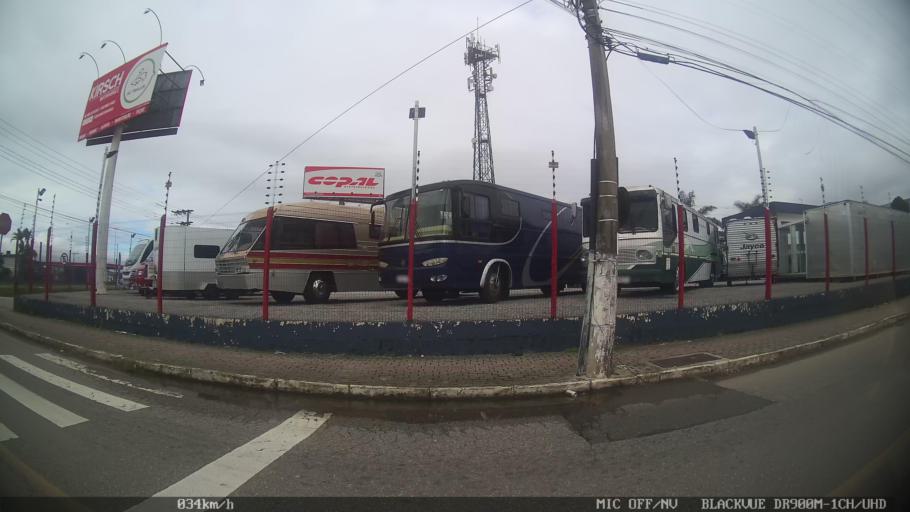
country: BR
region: Santa Catarina
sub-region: Biguacu
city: Biguacu
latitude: -27.5364
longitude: -48.6287
